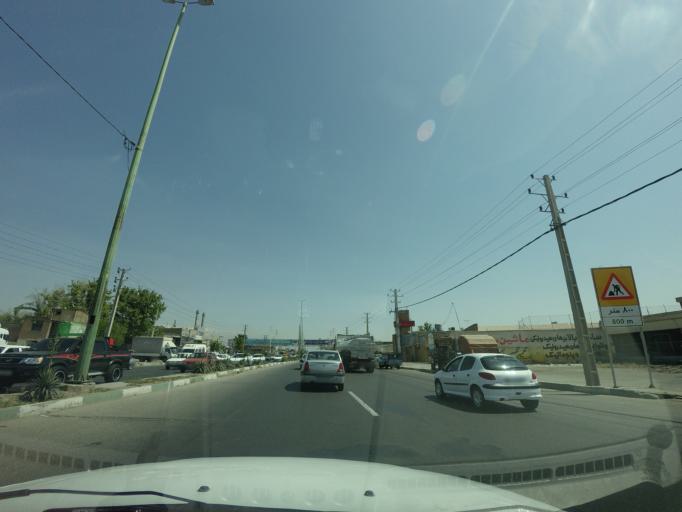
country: IR
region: Tehran
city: Eslamshahr
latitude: 35.5990
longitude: 51.2984
